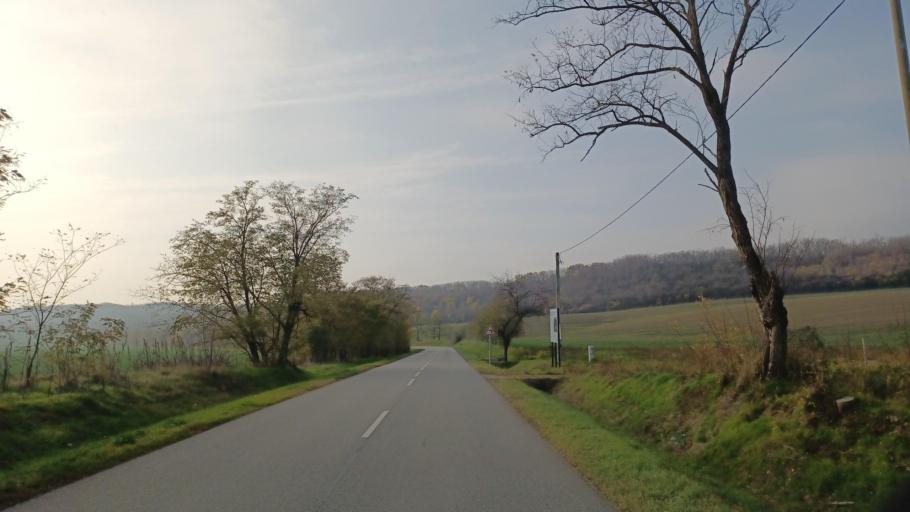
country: HU
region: Tolna
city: Dunaszentgyorgy
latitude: 46.5634
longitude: 18.7681
